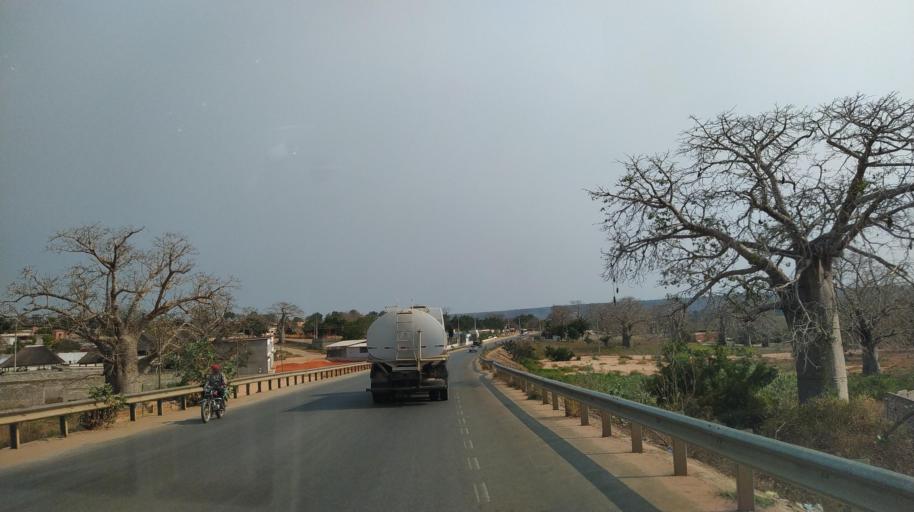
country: AO
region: Luanda
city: Luanda
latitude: -9.1440
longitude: 13.4153
